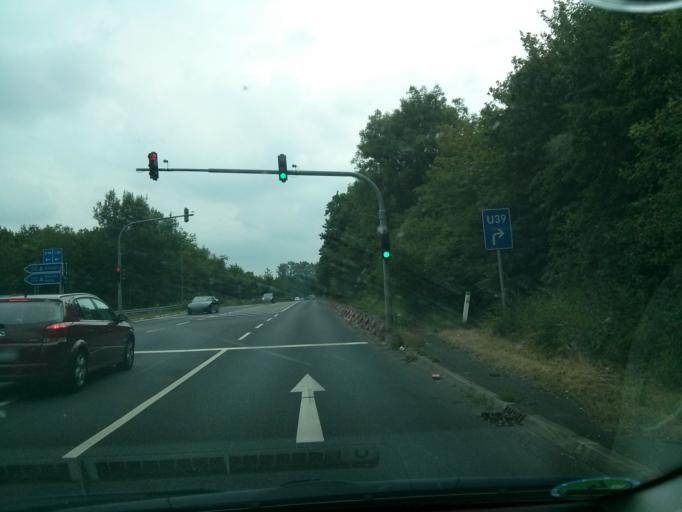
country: DE
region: North Rhine-Westphalia
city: Meckenheim
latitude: 50.6331
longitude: 7.0581
